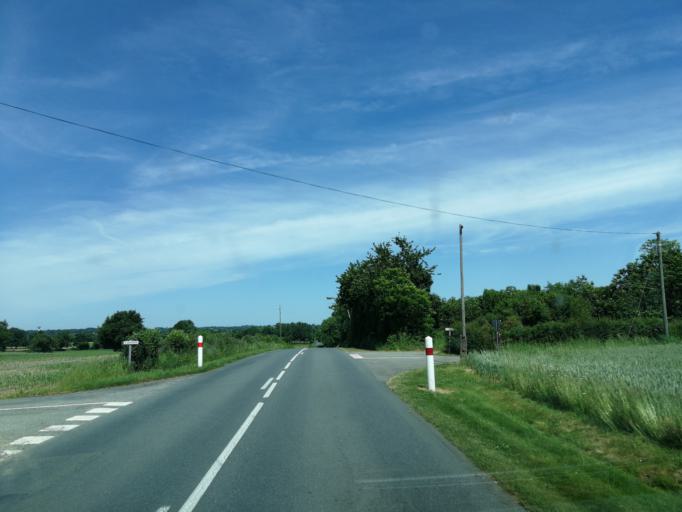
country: FR
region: Poitou-Charentes
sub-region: Departement des Deux-Sevres
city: La Foret-sur-Sevre
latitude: 46.7788
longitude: -0.6336
